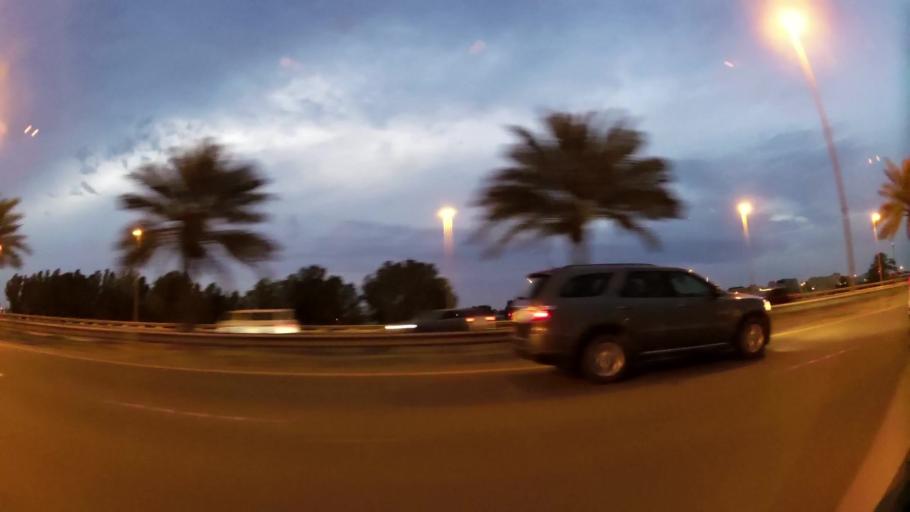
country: BH
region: Northern
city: Madinat `Isa
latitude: 26.1935
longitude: 50.5062
